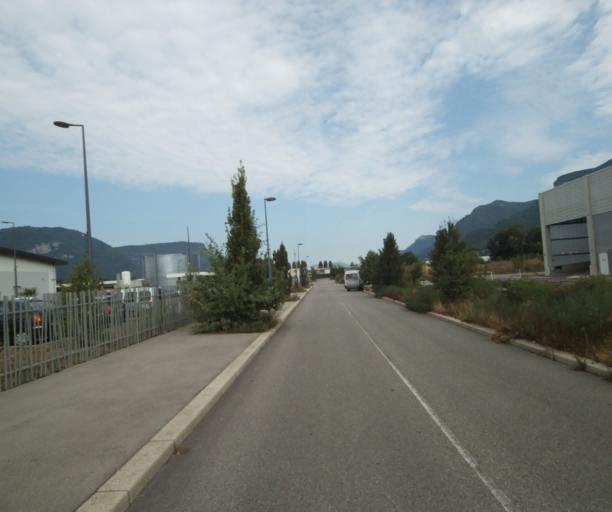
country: FR
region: Rhone-Alpes
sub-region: Departement de l'Isere
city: Fontanil-Cornillon
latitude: 45.2420
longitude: 5.6643
